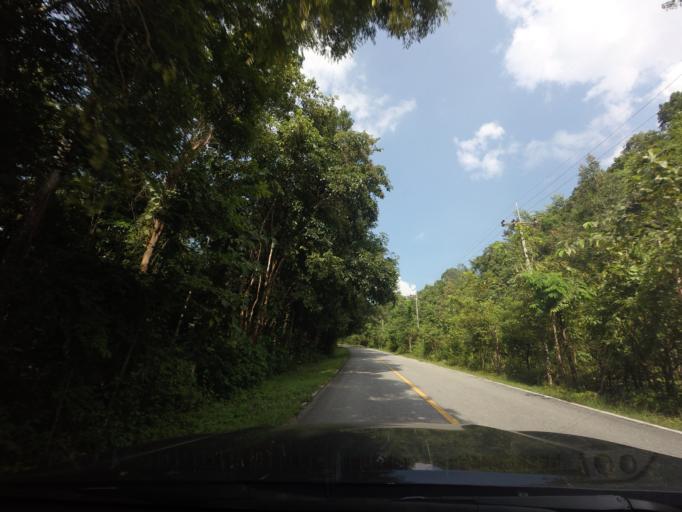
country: TH
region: Phitsanulok
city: Nakhon Thai
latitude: 17.0178
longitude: 100.9557
